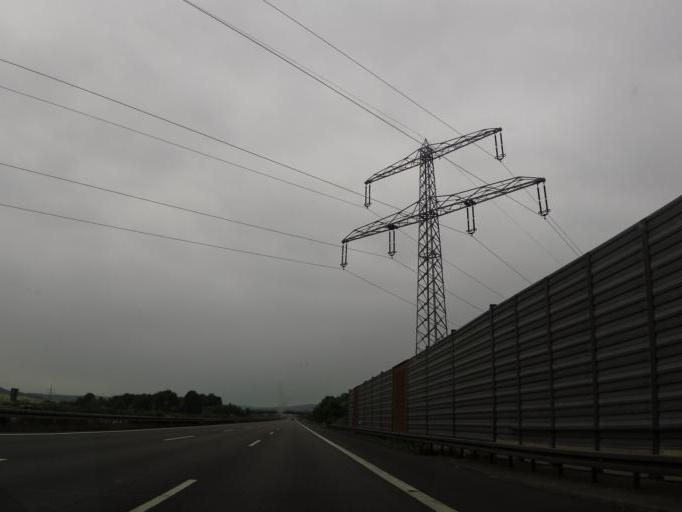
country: DE
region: Lower Saxony
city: Rosdorf
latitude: 51.4842
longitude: 9.8751
